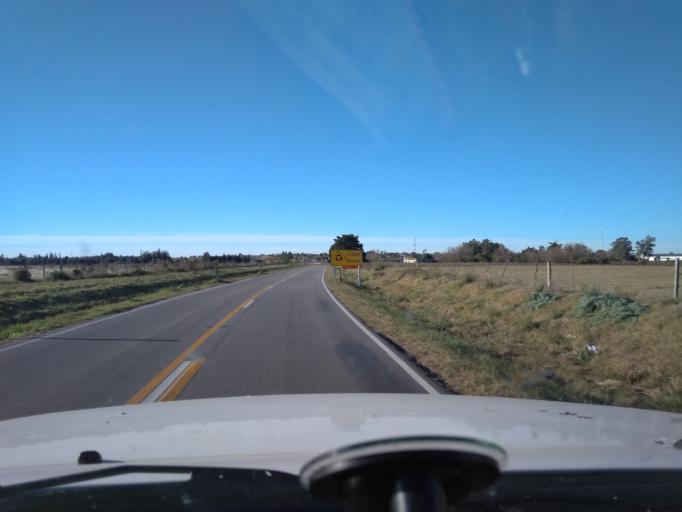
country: UY
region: Canelones
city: Santa Rosa
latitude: -34.5095
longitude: -56.0531
